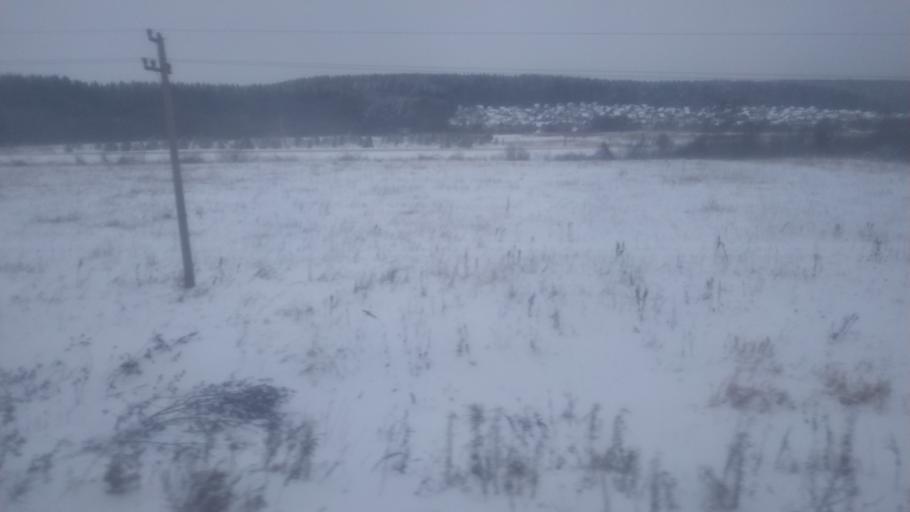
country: RU
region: Udmurtiya
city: Sigayevo
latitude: 56.4538
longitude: 53.6794
